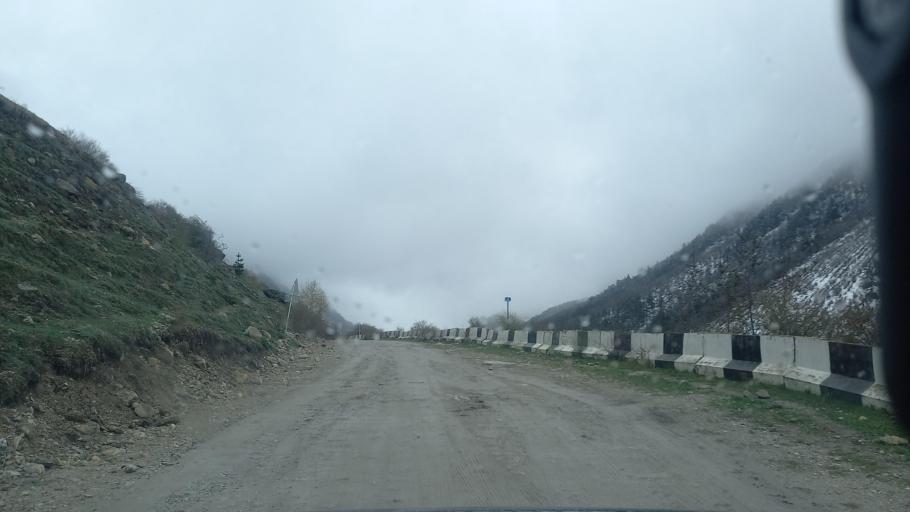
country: RU
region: Kabardino-Balkariya
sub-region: El'brusskiy Rayon
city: El'brus
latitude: 43.2271
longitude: 42.6627
